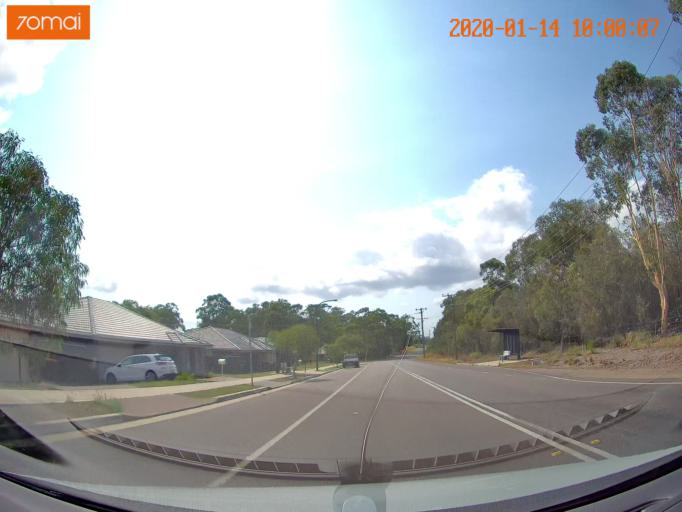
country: AU
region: New South Wales
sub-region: Lake Macquarie Shire
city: Dora Creek
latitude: -33.1209
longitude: 151.5298
